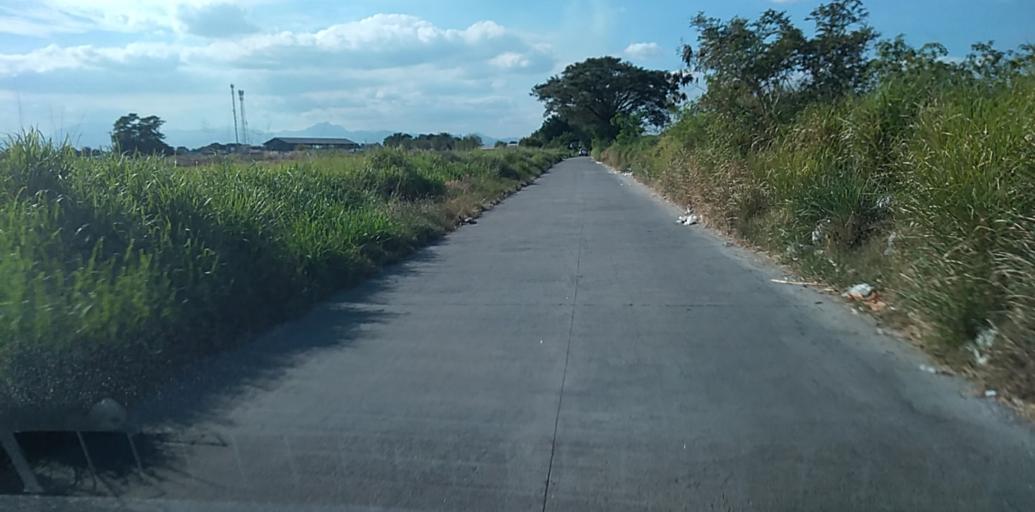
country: PH
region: Central Luzon
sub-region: Province of Pampanga
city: Acli
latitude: 15.1154
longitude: 120.6456
